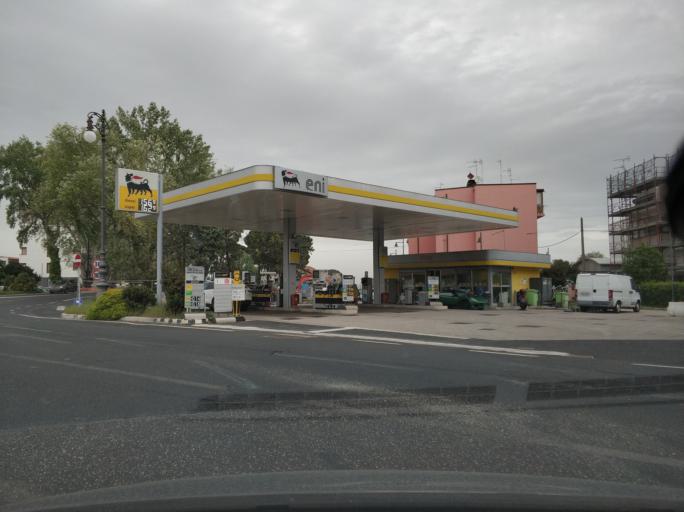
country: IT
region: Friuli Venezia Giulia
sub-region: Provincia di Gorizia
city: Grado
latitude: 45.6814
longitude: 13.3871
